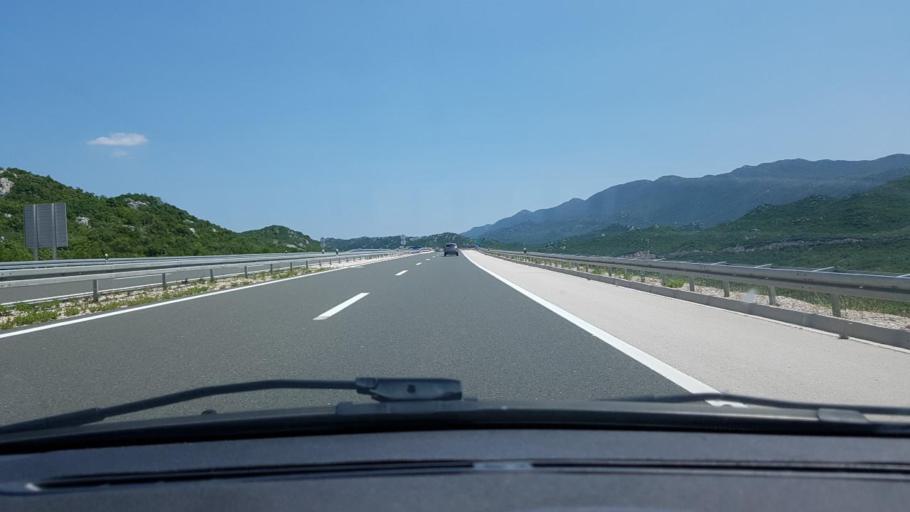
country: HR
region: Splitsko-Dalmatinska
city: Vrgorac
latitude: 43.2085
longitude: 17.2798
